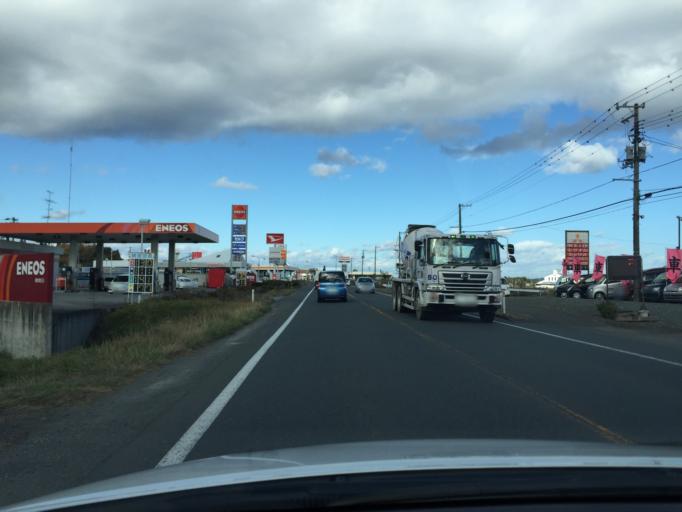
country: JP
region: Fukushima
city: Namie
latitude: 37.6159
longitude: 141.0022
